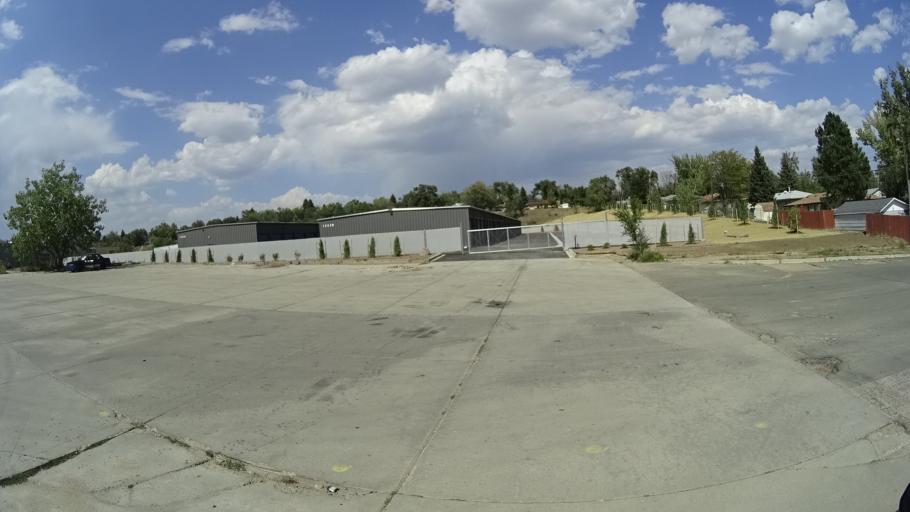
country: US
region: Colorado
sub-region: El Paso County
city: Colorado Springs
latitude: 38.8490
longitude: -104.7715
